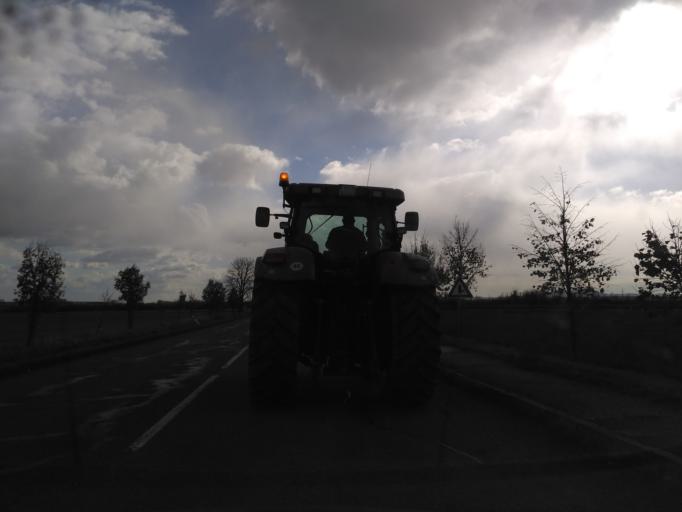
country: SK
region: Kosicky
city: Trebisov
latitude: 48.6414
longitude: 21.6833
